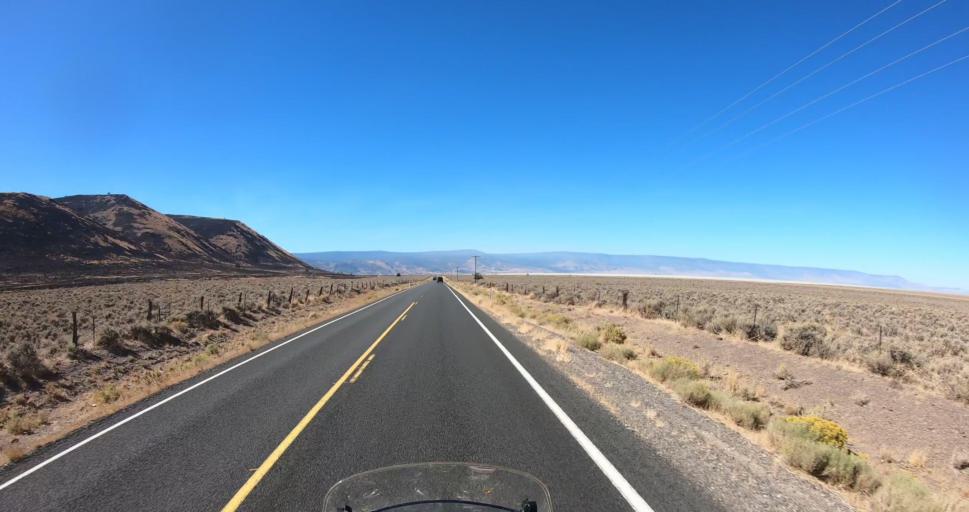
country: US
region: Oregon
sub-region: Lake County
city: Lakeview
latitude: 42.7211
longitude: -120.5971
